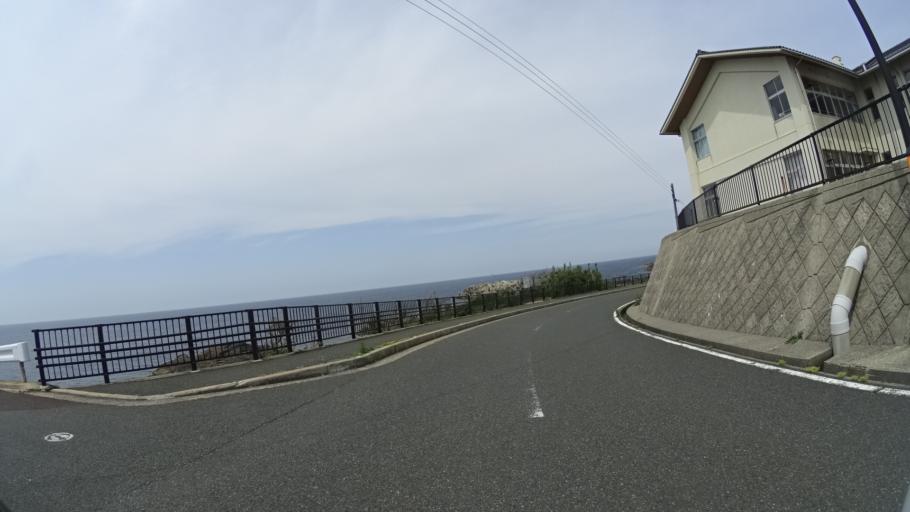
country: JP
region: Kyoto
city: Miyazu
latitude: 35.7390
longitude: 135.0884
